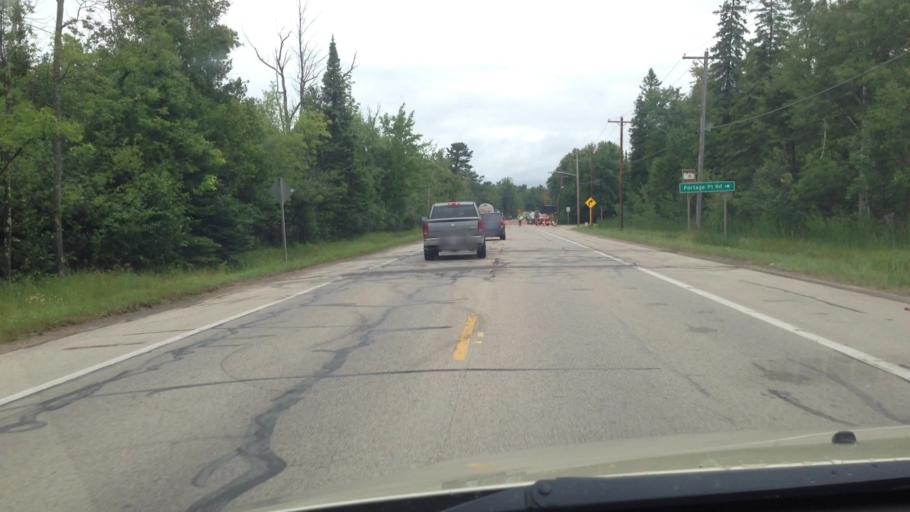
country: US
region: Michigan
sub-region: Delta County
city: Escanaba
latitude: 45.7001
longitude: -87.1013
